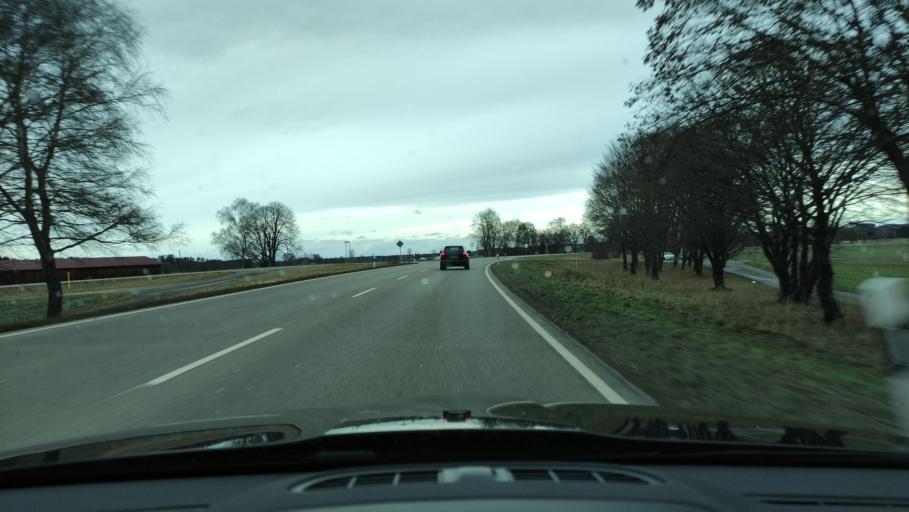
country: DE
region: Bavaria
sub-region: Swabia
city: Illertissen
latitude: 48.2240
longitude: 10.1298
